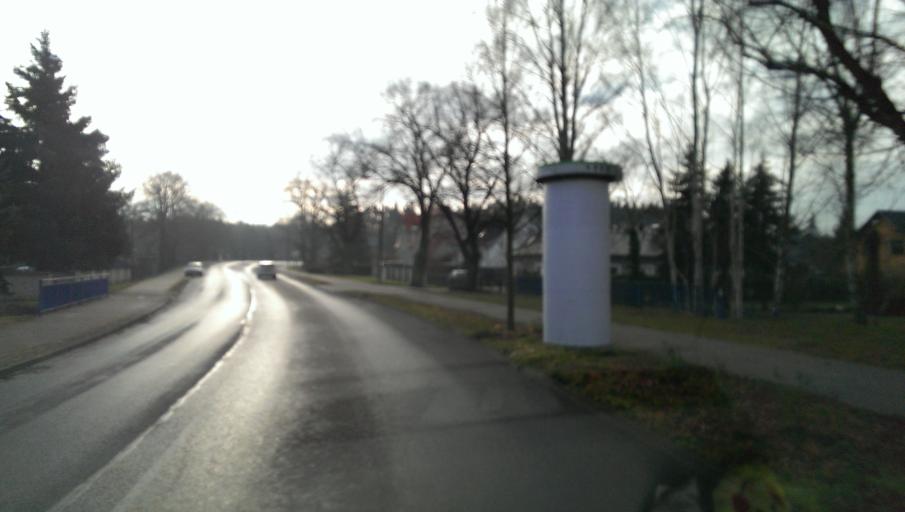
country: DE
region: Brandenburg
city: Luckenwalde
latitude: 52.0776
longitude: 13.1584
